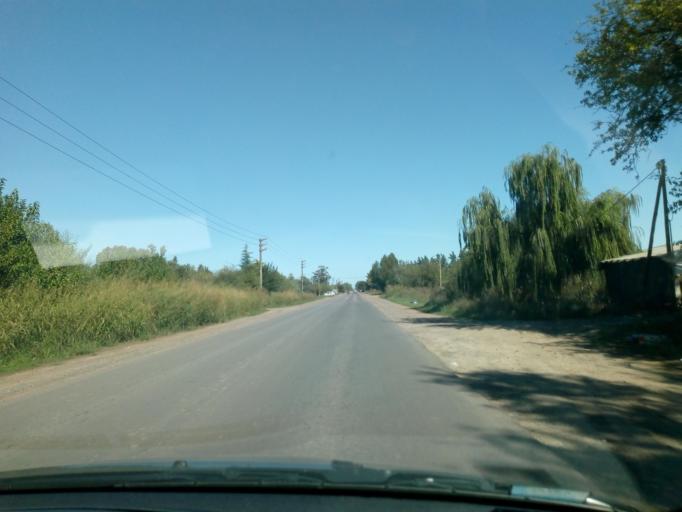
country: AR
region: Buenos Aires
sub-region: Partido de La Plata
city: La Plata
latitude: -35.0072
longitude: -58.0241
